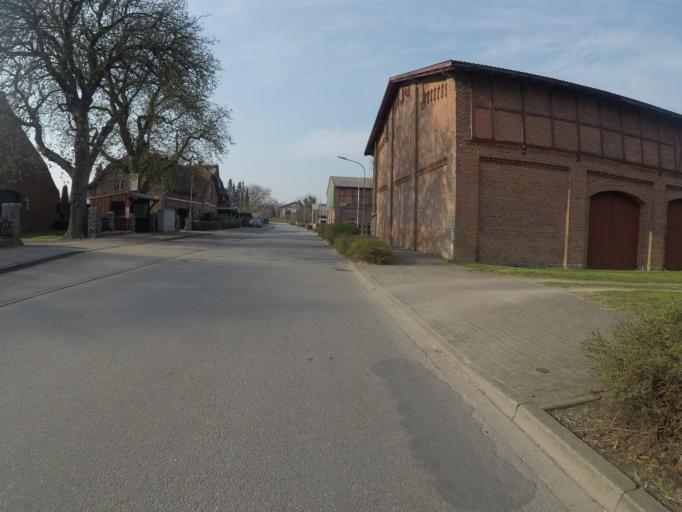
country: DE
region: Schleswig-Holstein
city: Kukels
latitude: 53.8951
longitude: 10.2389
